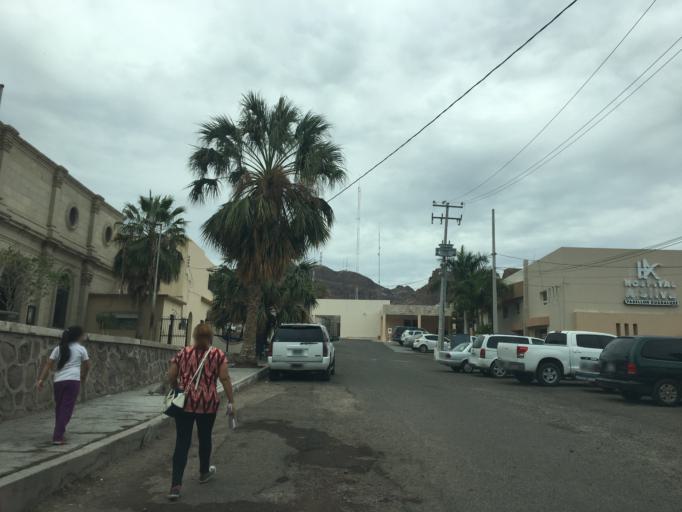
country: MX
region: Sonora
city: Heroica Guaymas
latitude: 27.9180
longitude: -110.9006
